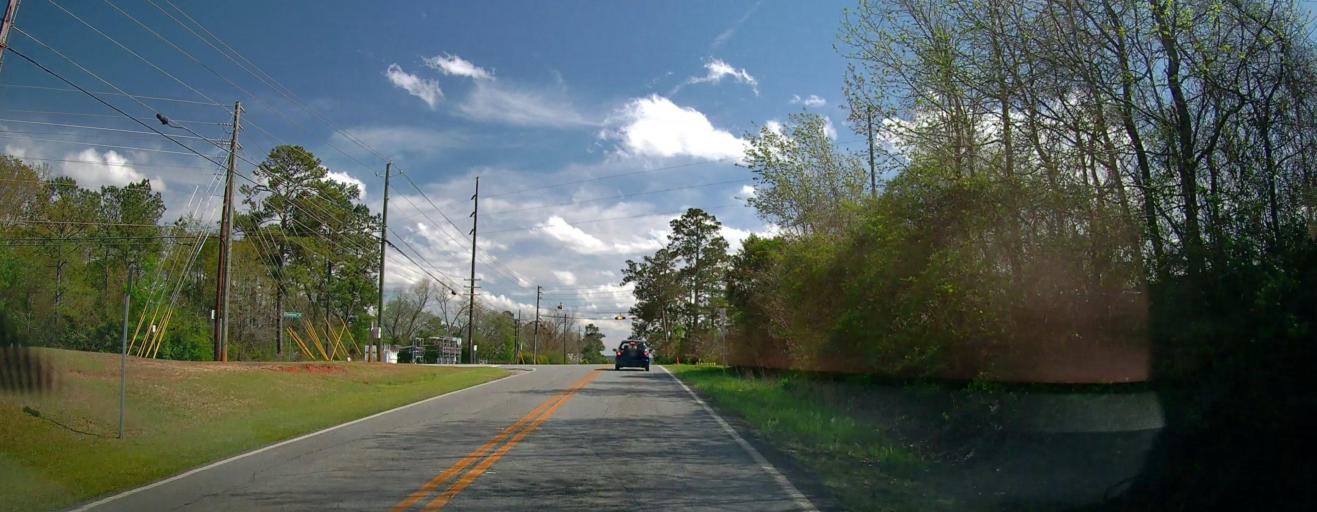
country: US
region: Georgia
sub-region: Bibb County
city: Macon
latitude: 32.8126
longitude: -83.5409
